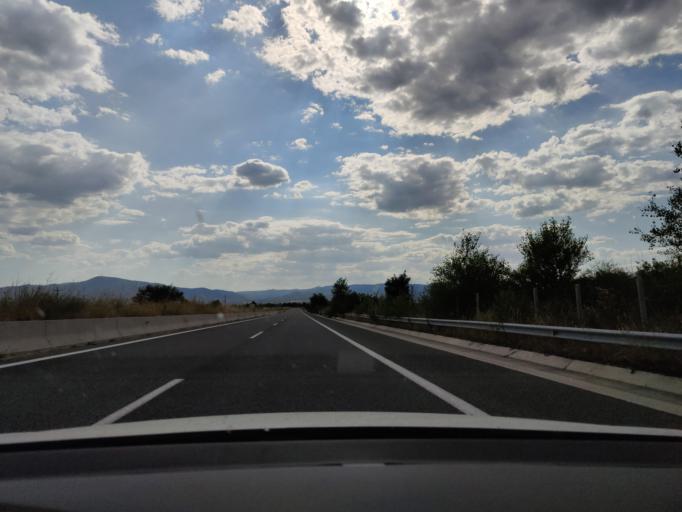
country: GR
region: Central Macedonia
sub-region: Nomos Serron
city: Provatas
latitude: 41.0685
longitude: 23.3617
